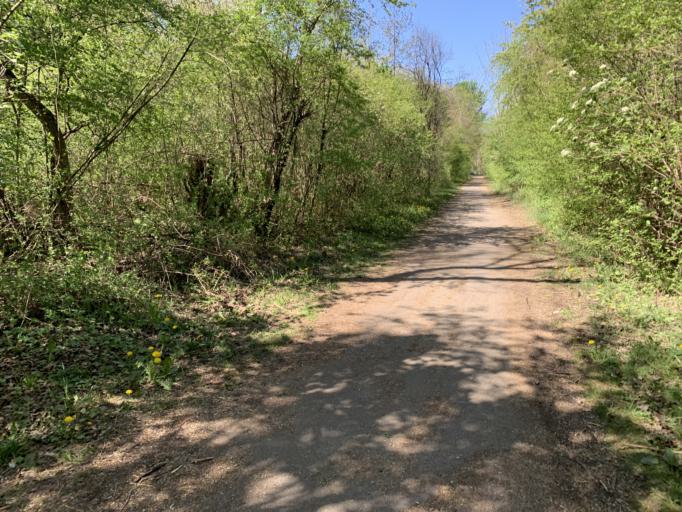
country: DE
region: Bavaria
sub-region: Swabia
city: Gersthofen
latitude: 48.4290
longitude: 10.8915
